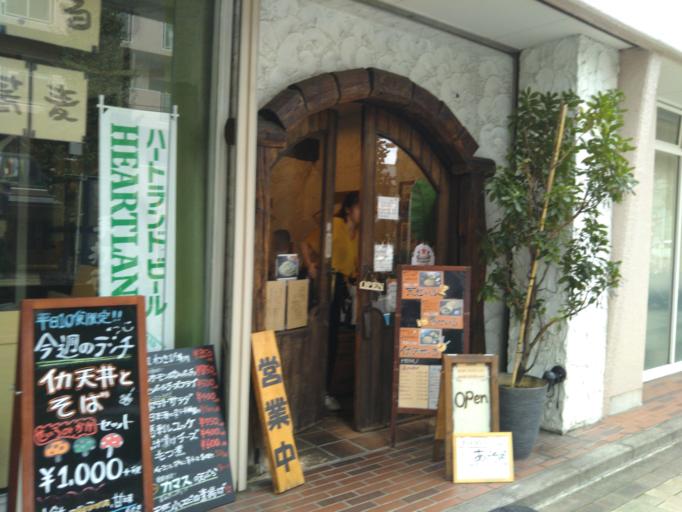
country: JP
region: Tokyo
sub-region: Machida-shi
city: Machida
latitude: 35.5684
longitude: 139.3919
